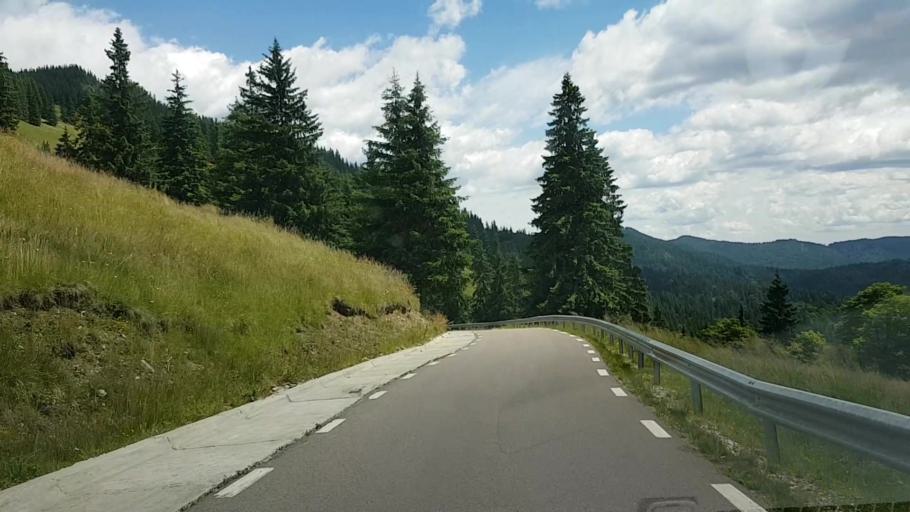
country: RO
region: Suceava
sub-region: Municipiul Campulung Moldovenesc
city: Campulung Moldovenesc
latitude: 47.4377
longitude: 25.5547
